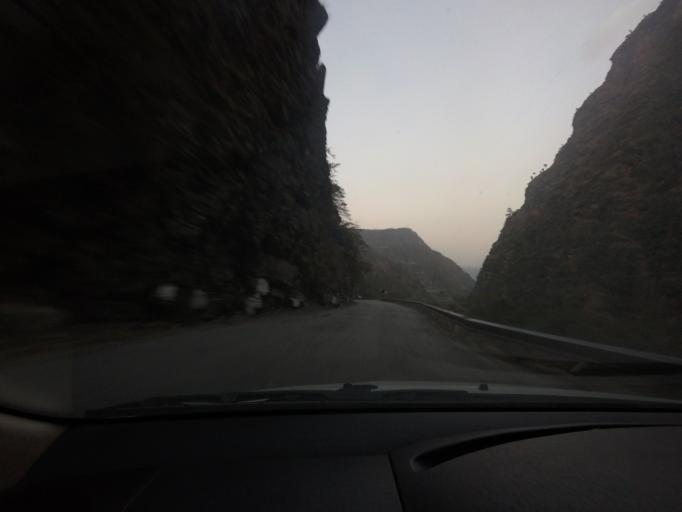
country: IN
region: Himachal Pradesh
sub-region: Mandi
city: Pandoh
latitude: 31.6921
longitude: 77.1335
